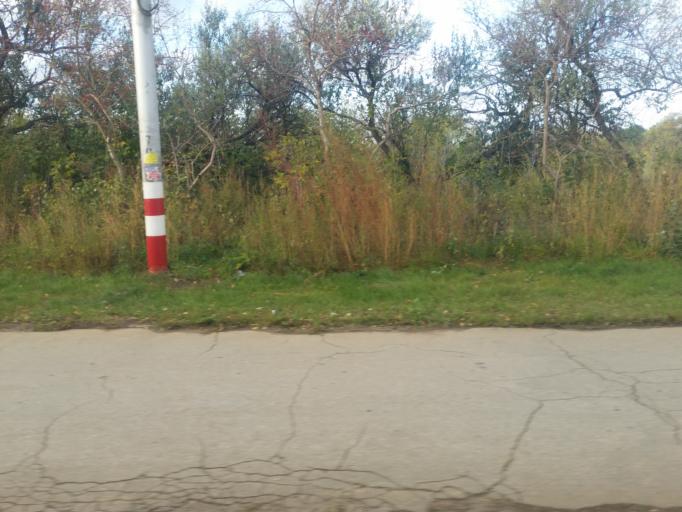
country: RU
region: Ulyanovsk
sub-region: Ulyanovskiy Rayon
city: Ulyanovsk
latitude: 54.3154
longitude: 48.3856
